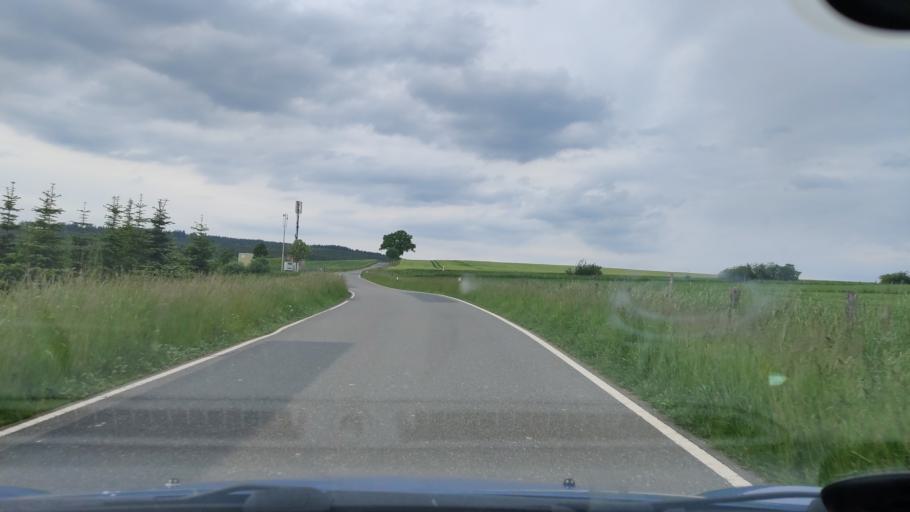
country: DE
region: Lower Saxony
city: Eimen
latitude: 51.8729
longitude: 9.8203
